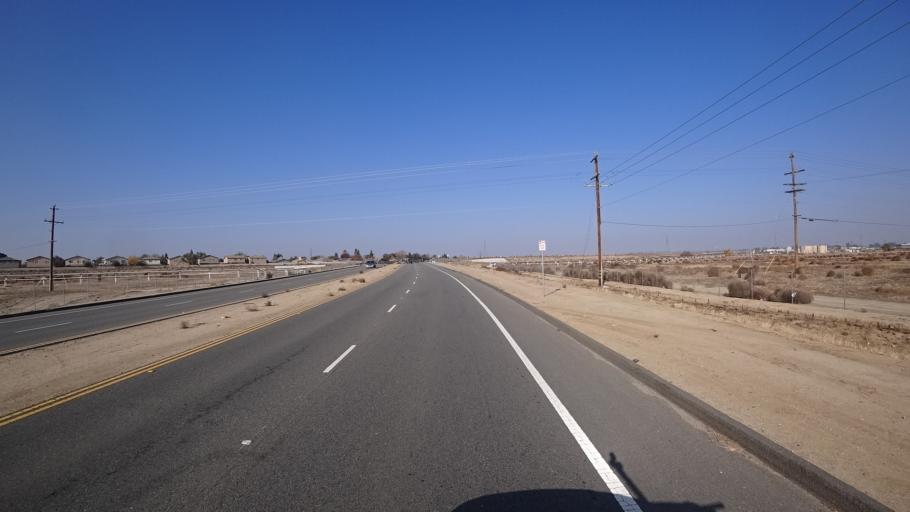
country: US
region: California
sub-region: Kern County
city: Greenacres
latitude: 35.3902
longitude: -119.0655
